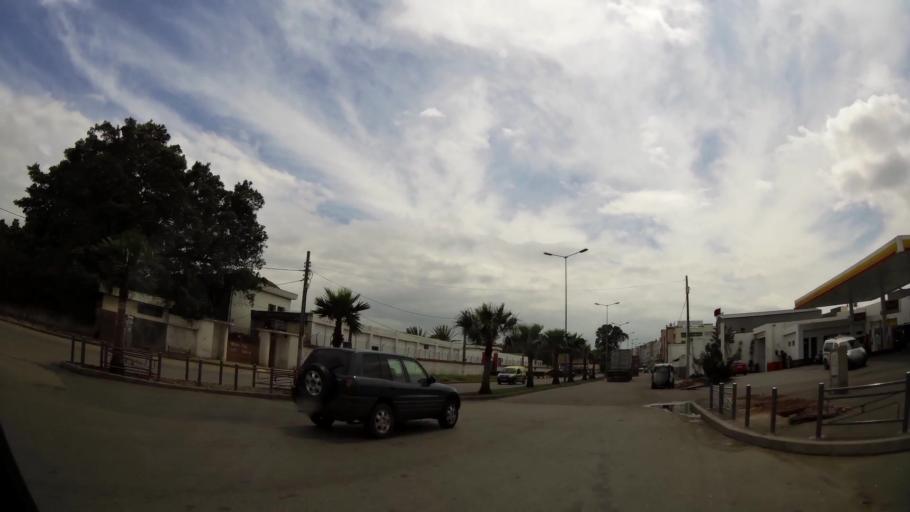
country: MA
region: Grand Casablanca
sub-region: Casablanca
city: Casablanca
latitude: 33.5895
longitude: -7.5730
